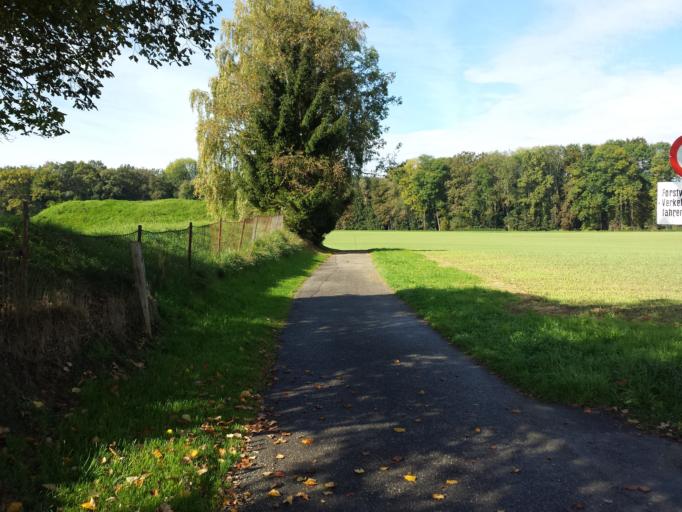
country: CH
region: Thurgau
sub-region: Arbon District
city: Salmsach
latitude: 47.5651
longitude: 9.3582
